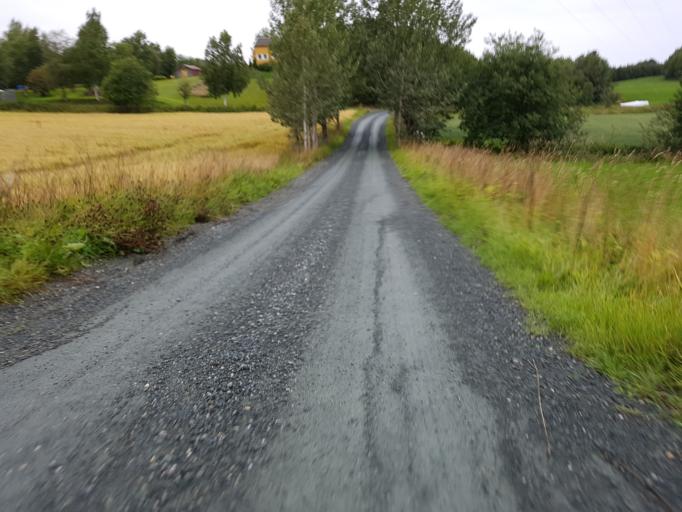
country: NO
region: Sor-Trondelag
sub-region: Trondheim
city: Trondheim
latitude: 63.4006
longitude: 10.4632
